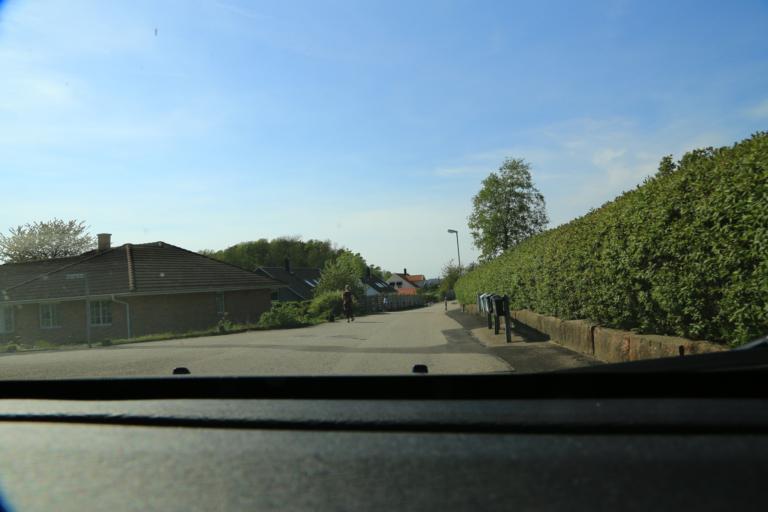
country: SE
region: Halland
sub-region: Varbergs Kommun
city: Varberg
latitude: 57.1364
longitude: 12.2881
